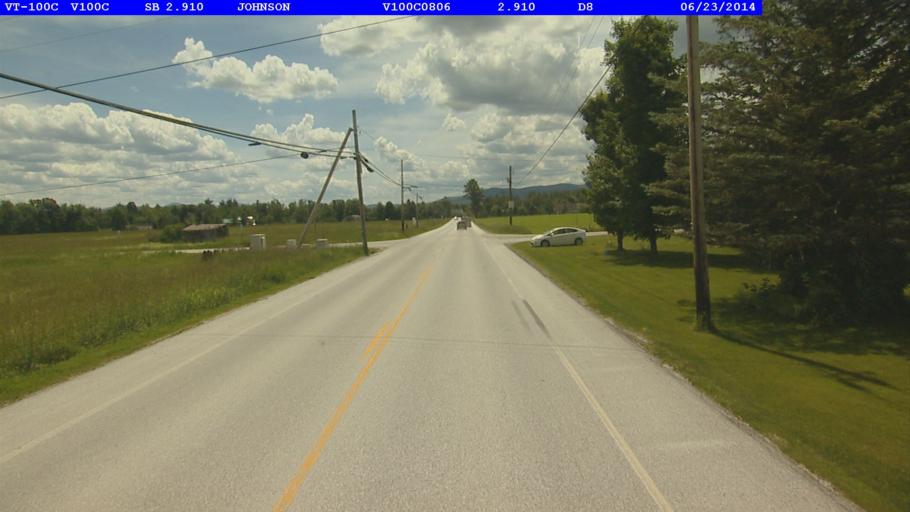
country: US
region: Vermont
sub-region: Lamoille County
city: Johnson
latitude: 44.6544
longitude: -72.6315
